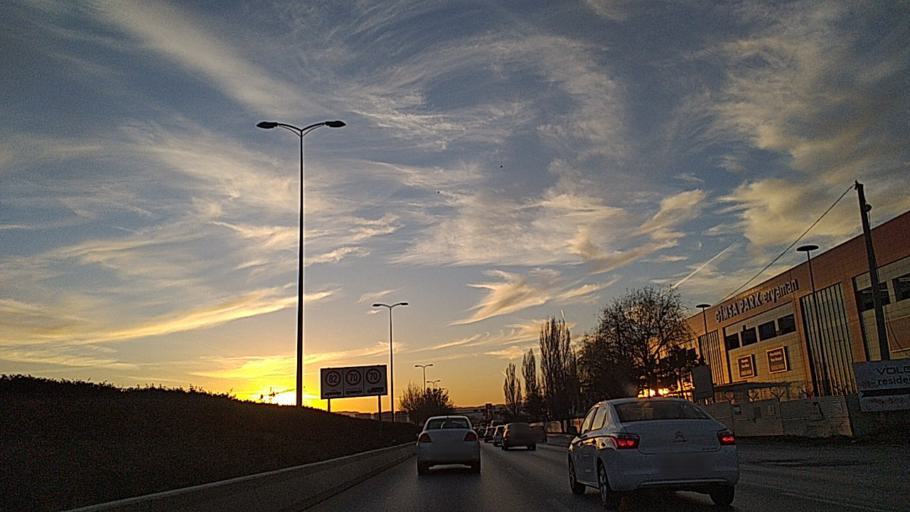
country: TR
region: Ankara
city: Etimesgut
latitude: 39.9633
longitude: 32.6524
